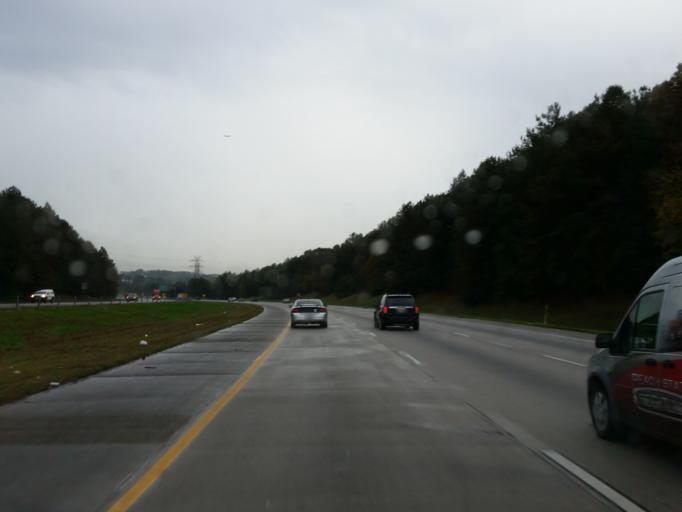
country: US
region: Georgia
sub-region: Clayton County
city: Conley
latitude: 33.6547
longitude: -84.3247
